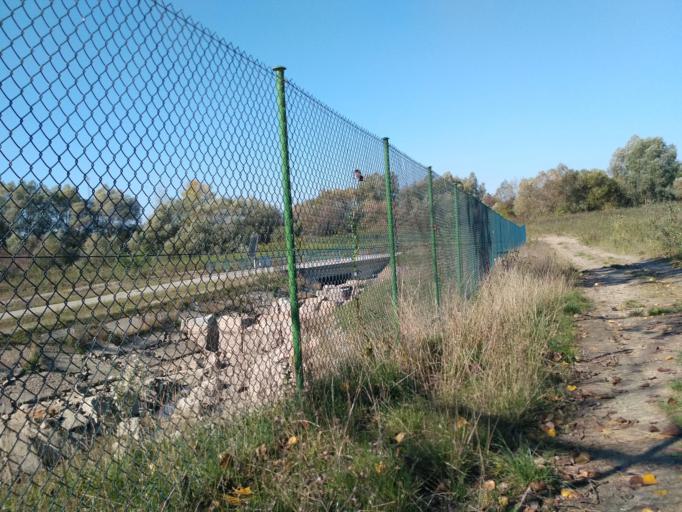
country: PL
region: Subcarpathian Voivodeship
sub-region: Powiat debicki
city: Pilzno
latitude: 49.9757
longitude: 21.3157
